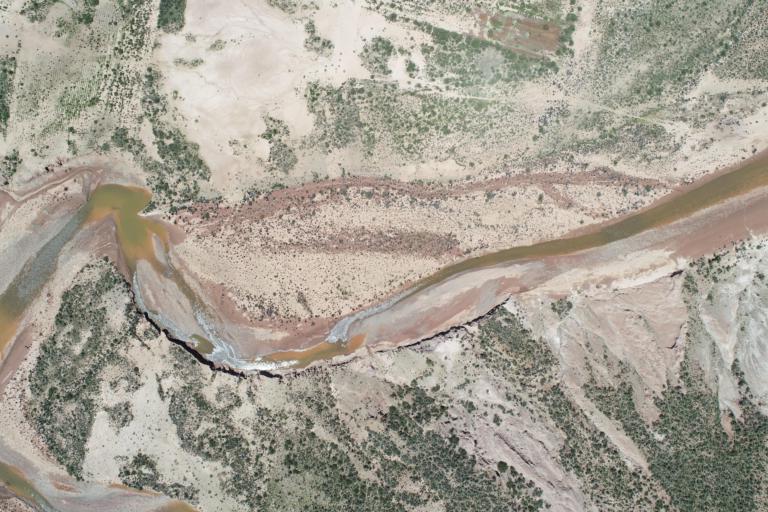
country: BO
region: La Paz
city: Curahuara de Carangas
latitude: -17.3139
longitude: -68.4955
